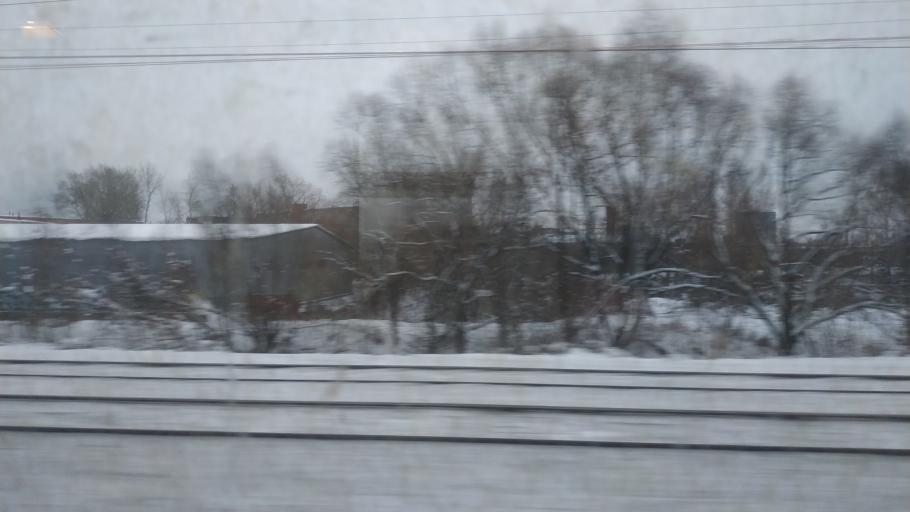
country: RU
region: Moskovskaya
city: Shcherbinka
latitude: 55.4957
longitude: 37.5580
